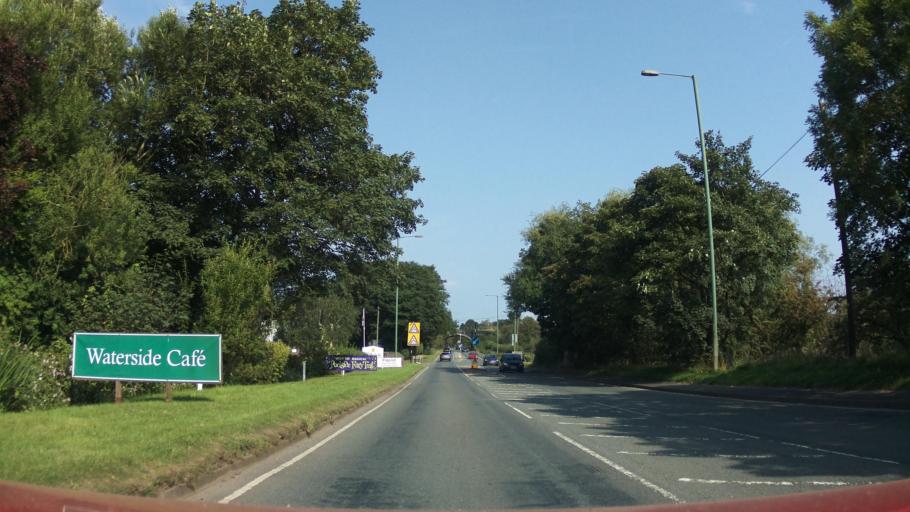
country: GB
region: England
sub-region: Walsall
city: Streetly
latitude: 52.5965
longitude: -1.8914
